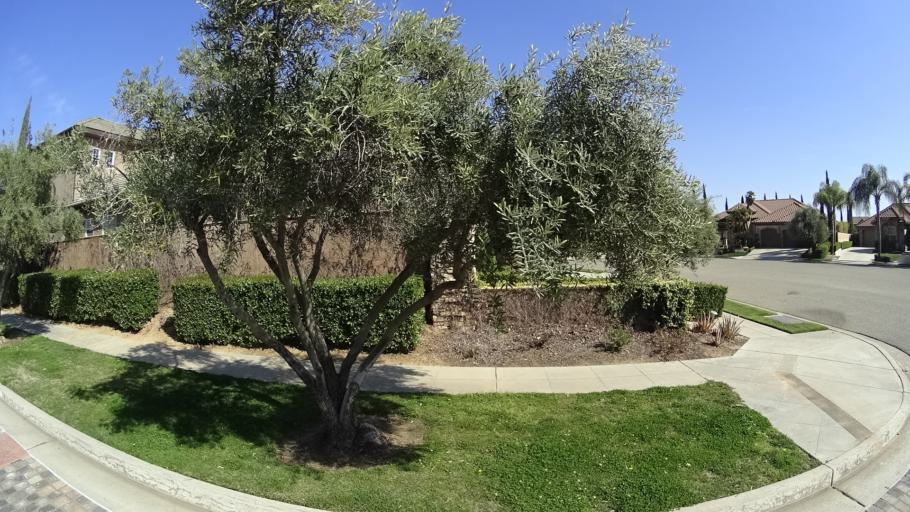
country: US
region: California
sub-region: Fresno County
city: Clovis
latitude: 36.8951
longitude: -119.7430
